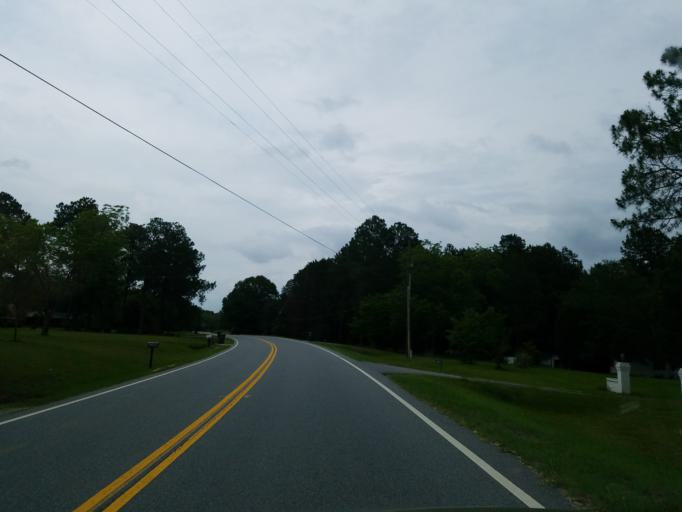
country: US
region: Georgia
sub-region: Crisp County
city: Cordele
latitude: 32.0162
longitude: -83.7321
